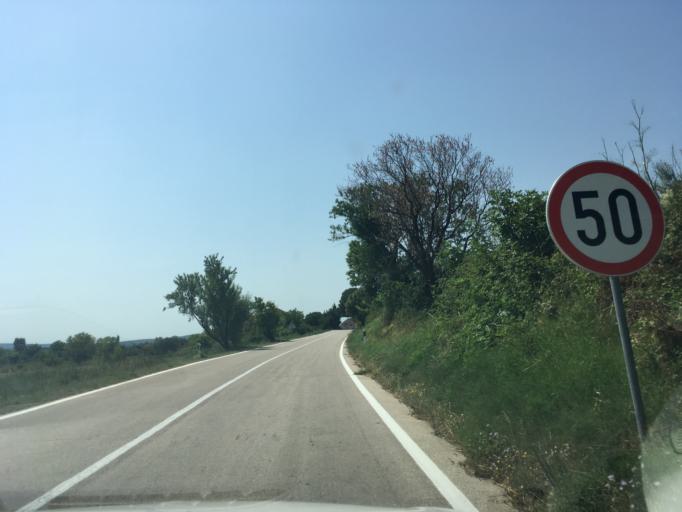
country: HR
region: Sibensko-Kniniska
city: Zaton
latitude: 43.9250
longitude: 15.8054
